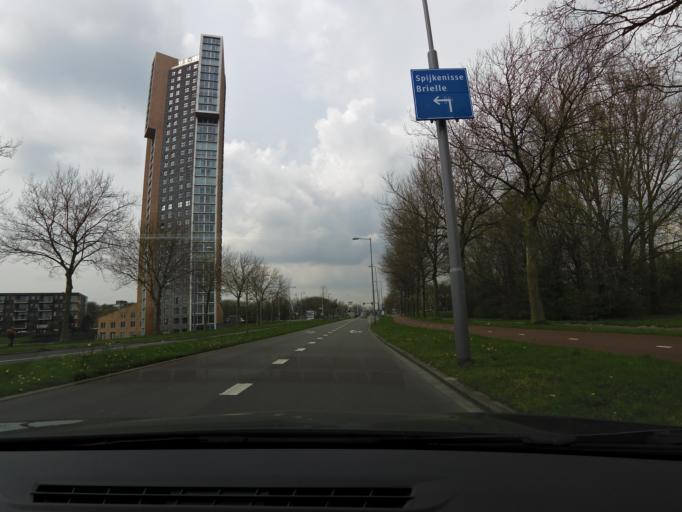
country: NL
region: South Holland
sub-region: Gemeente Spijkenisse
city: Spijkenisse
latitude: 51.8614
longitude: 4.3538
